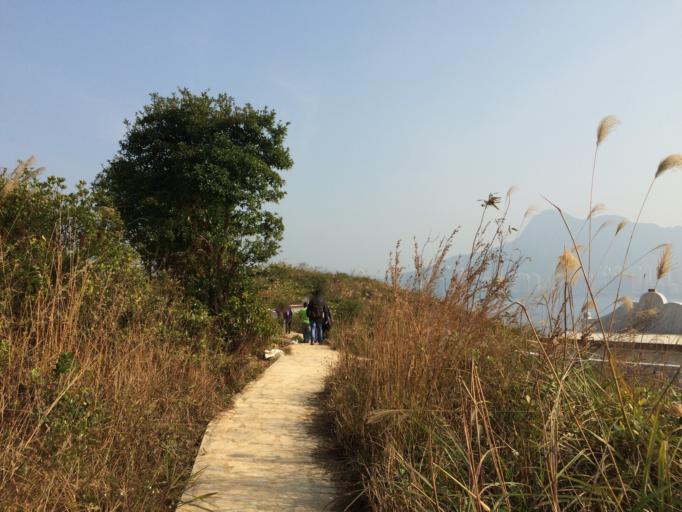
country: HK
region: Tai Po
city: Tai Po
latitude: 22.4507
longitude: 114.2186
